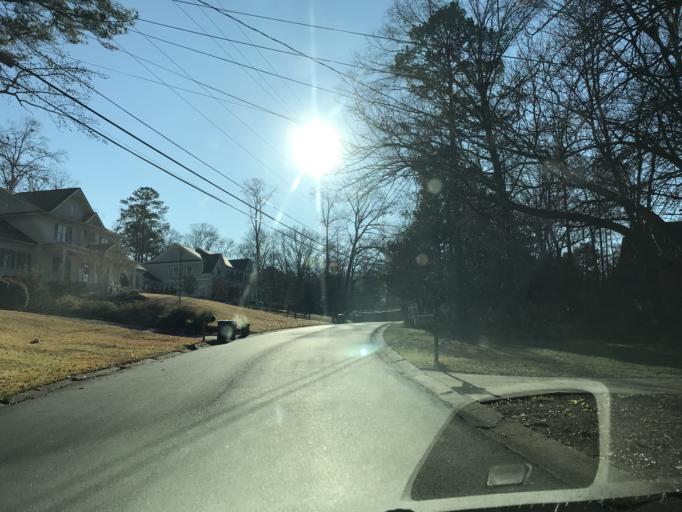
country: US
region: Georgia
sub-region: DeKalb County
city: North Atlanta
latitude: 33.8862
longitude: -84.3410
